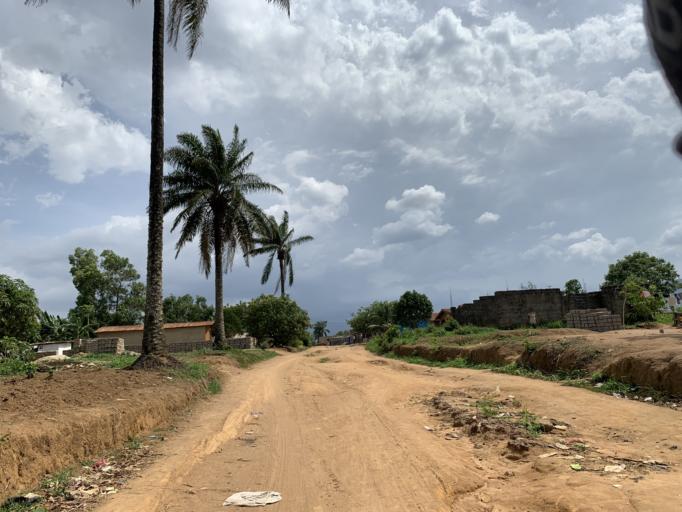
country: SL
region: Western Area
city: Waterloo
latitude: 8.3481
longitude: -13.0505
